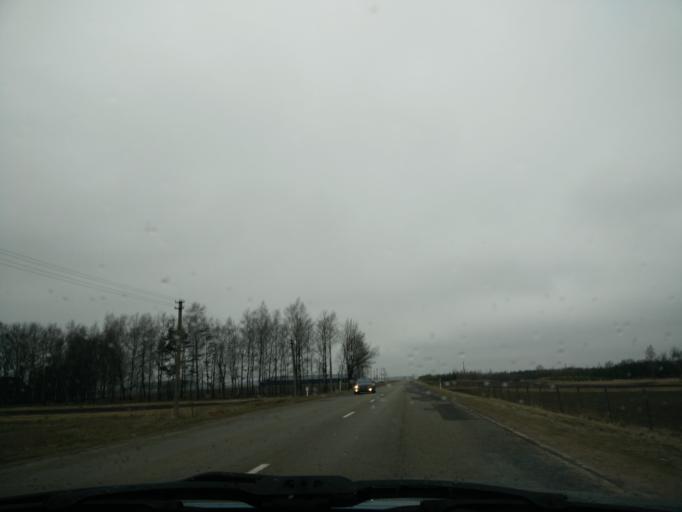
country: LT
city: Raseiniai
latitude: 55.3676
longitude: 23.0787
